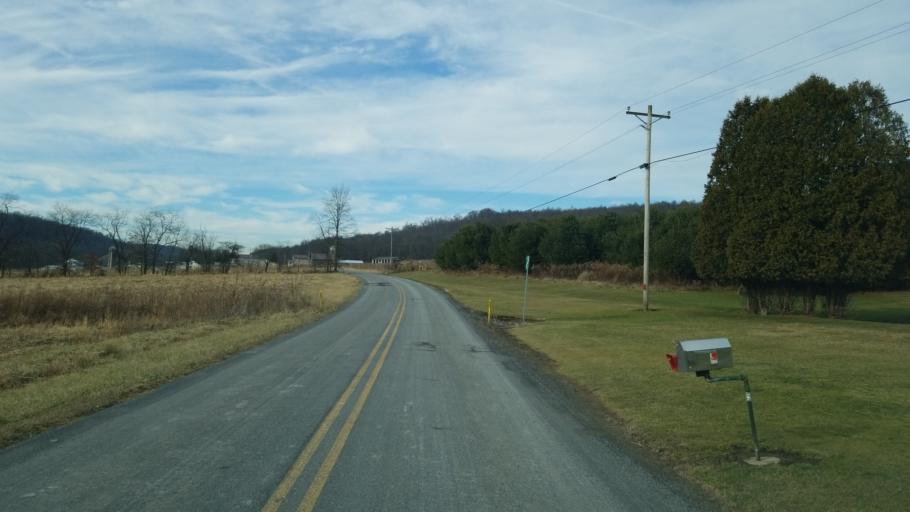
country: US
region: Pennsylvania
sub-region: Jefferson County
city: Punxsutawney
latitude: 40.8394
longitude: -79.1287
